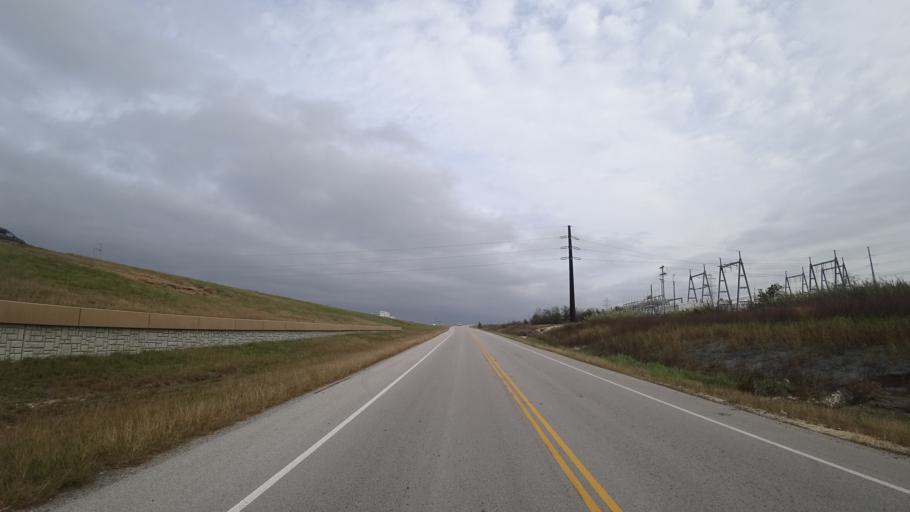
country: US
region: Texas
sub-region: Travis County
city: Manor
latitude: 30.3705
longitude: -97.5825
